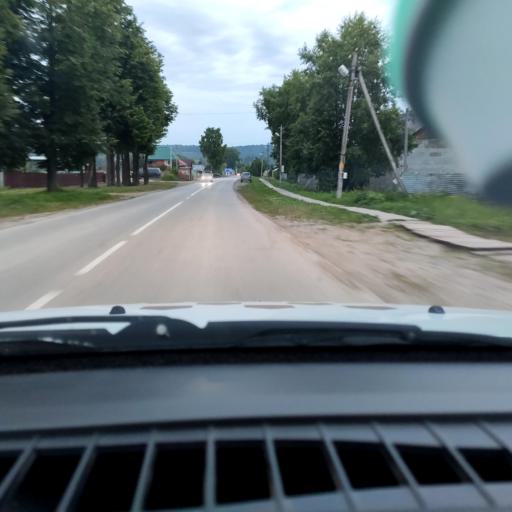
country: RU
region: Perm
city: Bershet'
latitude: 57.7326
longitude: 56.3681
